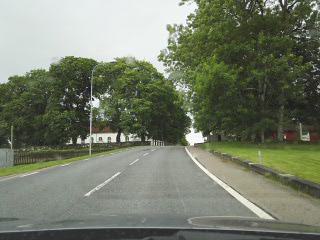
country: SE
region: Joenkoeping
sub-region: Vetlanda Kommun
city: Landsbro
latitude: 57.3215
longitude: 14.8685
